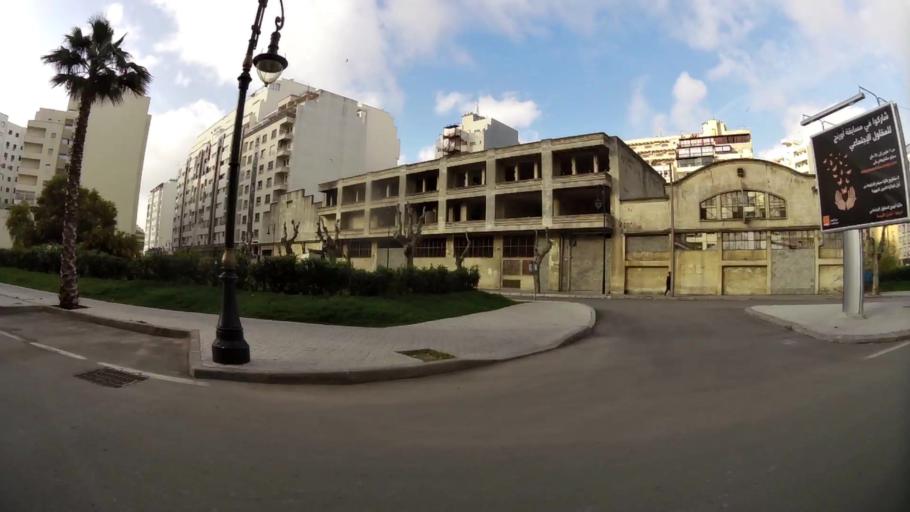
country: MA
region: Tanger-Tetouan
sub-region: Tanger-Assilah
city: Tangier
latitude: 35.7732
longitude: -5.7948
